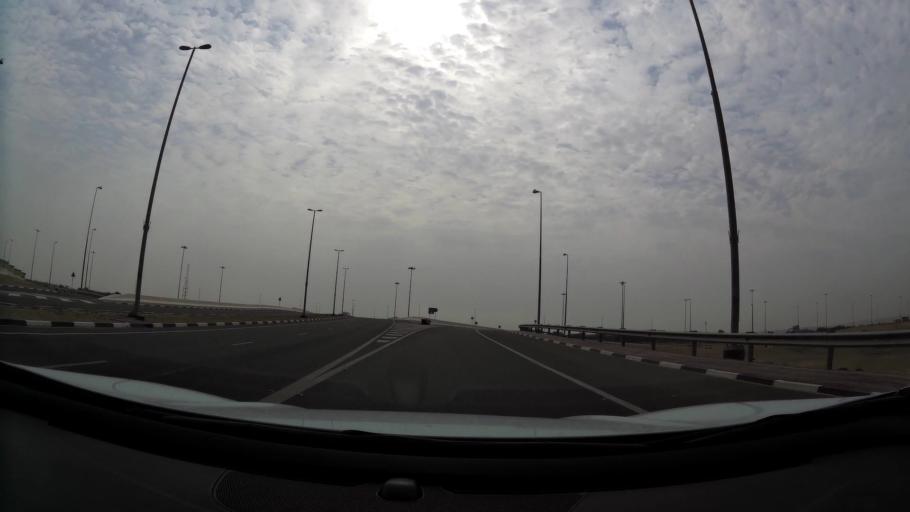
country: AE
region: Abu Dhabi
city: Abu Dhabi
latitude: 24.6869
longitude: 54.7714
